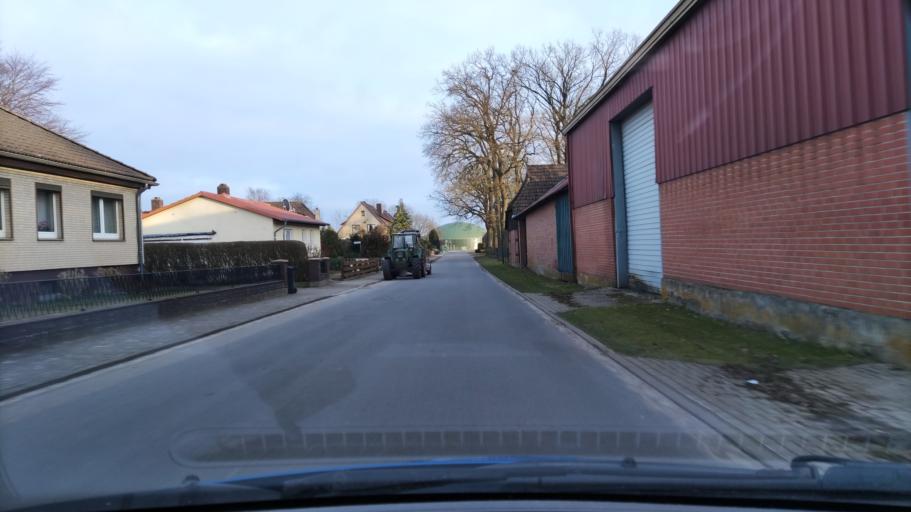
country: DE
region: Lower Saxony
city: Gerdau
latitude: 52.9719
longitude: 10.3986
